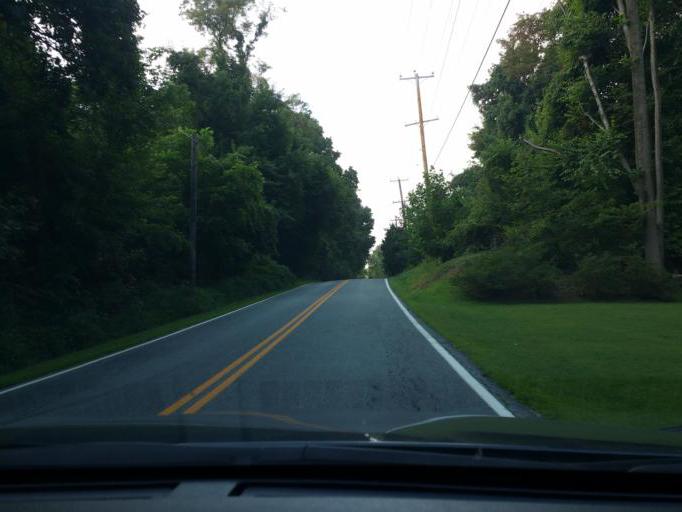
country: US
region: Maryland
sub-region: Cecil County
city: Rising Sun
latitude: 39.6475
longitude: -76.1241
